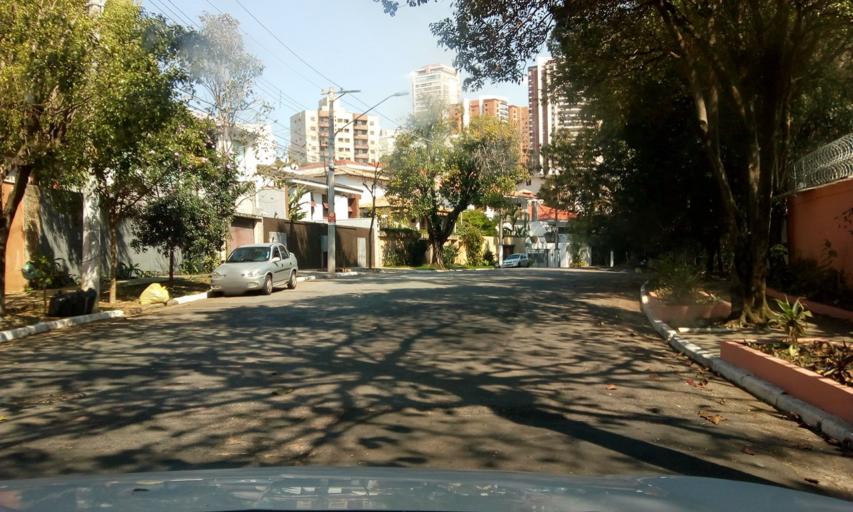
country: BR
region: Sao Paulo
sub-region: Osasco
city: Osasco
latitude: -23.5288
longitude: -46.7160
